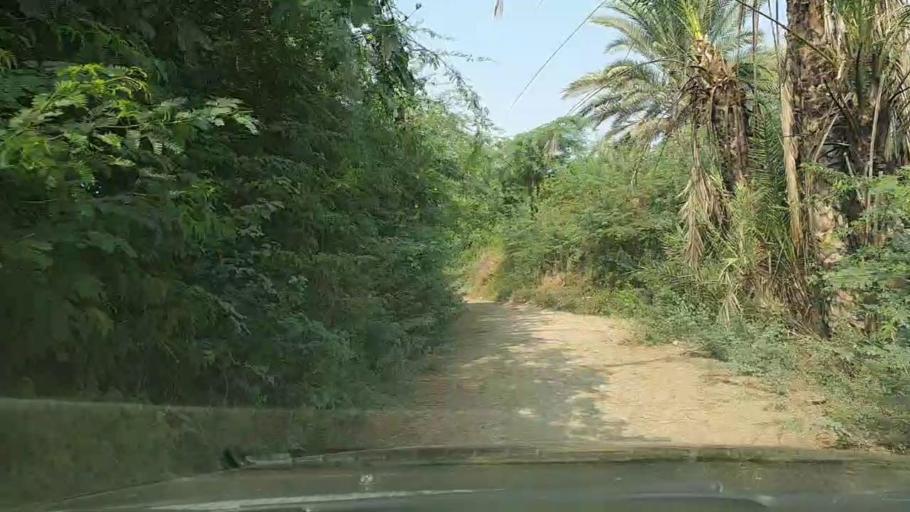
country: PK
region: Sindh
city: Mirpur Batoro
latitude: 24.6825
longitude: 68.2369
